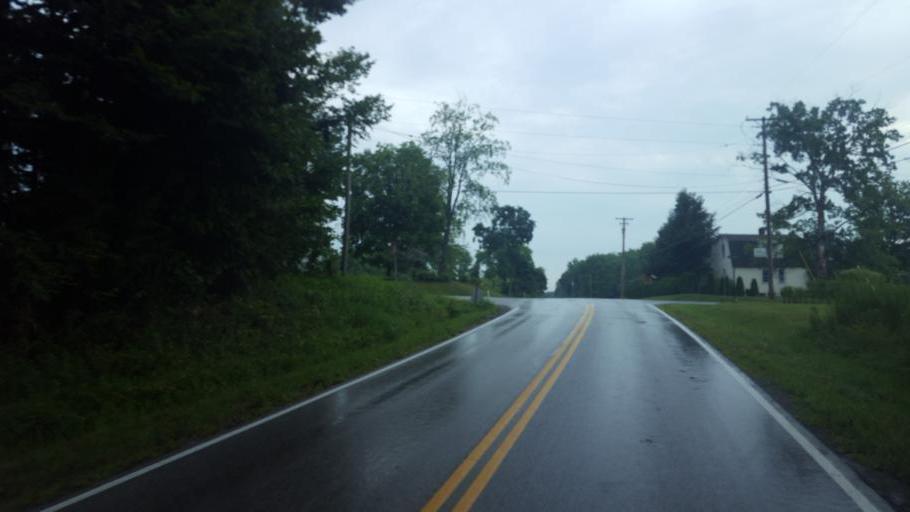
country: US
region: Ohio
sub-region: Geauga County
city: Middlefield
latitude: 41.4146
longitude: -81.0167
